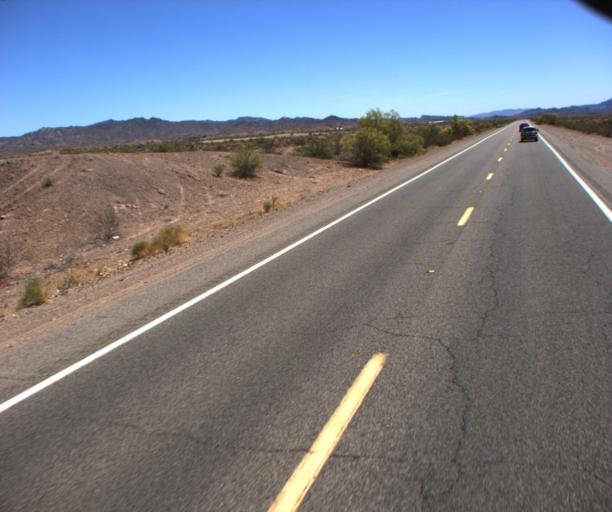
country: US
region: Arizona
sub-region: Mohave County
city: Lake Havasu City
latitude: 34.4231
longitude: -114.2039
